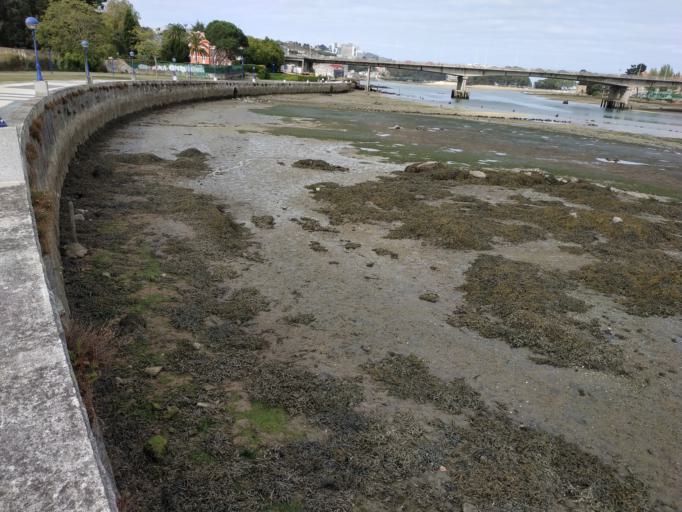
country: ES
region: Galicia
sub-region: Provincia da Coruna
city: Culleredo
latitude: 43.3297
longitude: -8.3817
